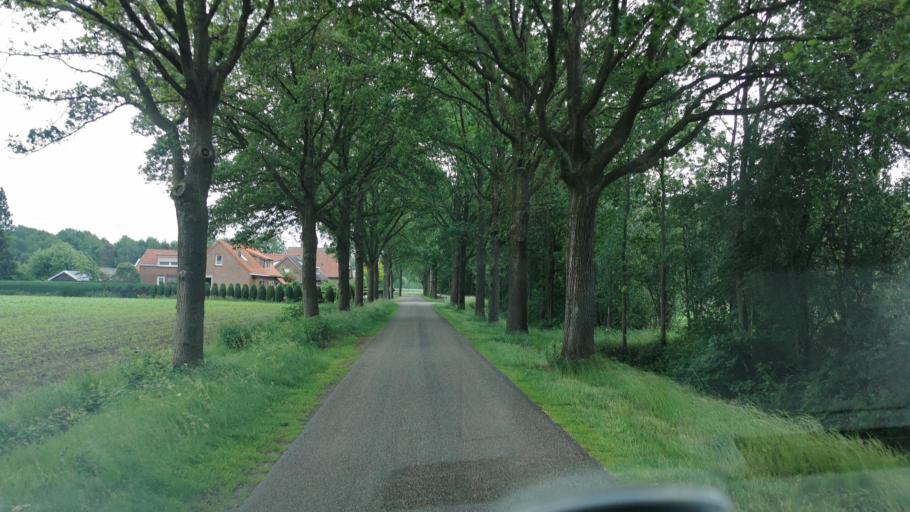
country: DE
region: North Rhine-Westphalia
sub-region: Regierungsbezirk Munster
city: Gronau
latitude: 52.2290
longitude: 7.0257
